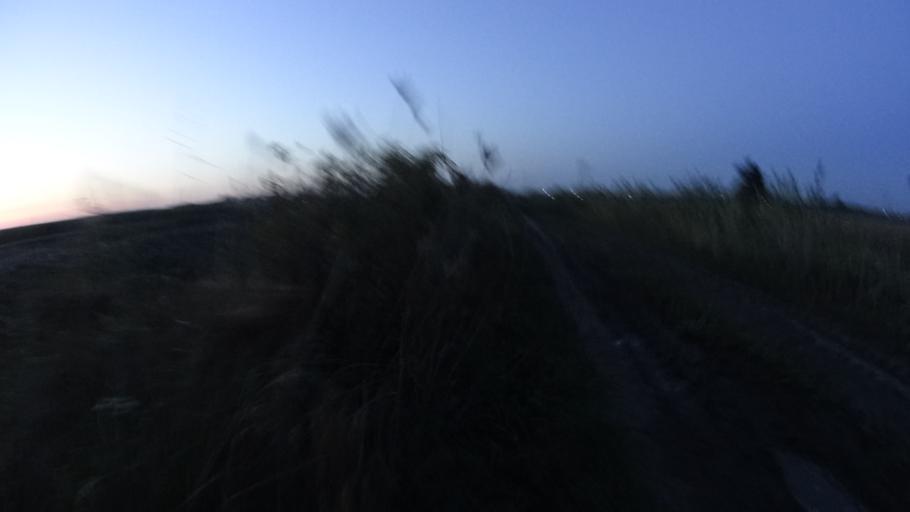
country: PL
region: Masovian Voivodeship
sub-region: Powiat warszawski zachodni
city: Ozarow Mazowiecki
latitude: 52.2245
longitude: 20.7912
